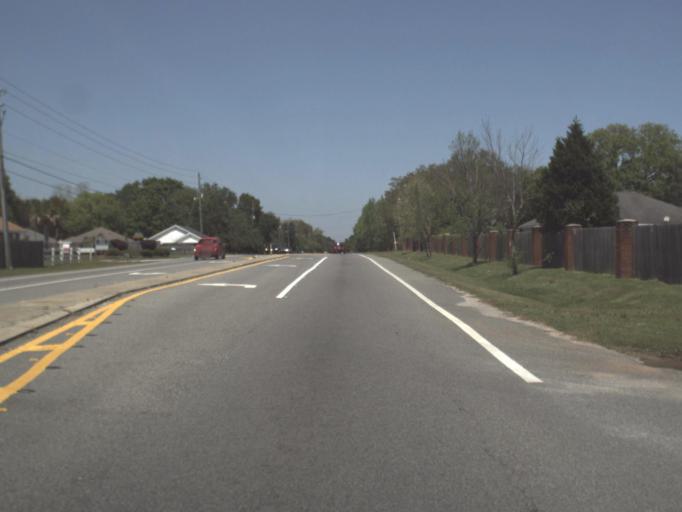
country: US
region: Florida
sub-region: Escambia County
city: Bellview
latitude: 30.4775
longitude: -87.3236
